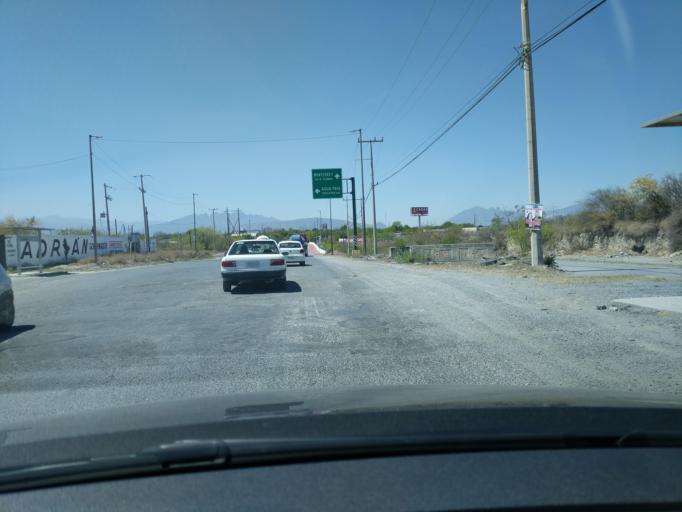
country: MX
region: Nuevo Leon
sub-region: Apodaca
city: Artemio Trevino
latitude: 25.8173
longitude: -100.1492
